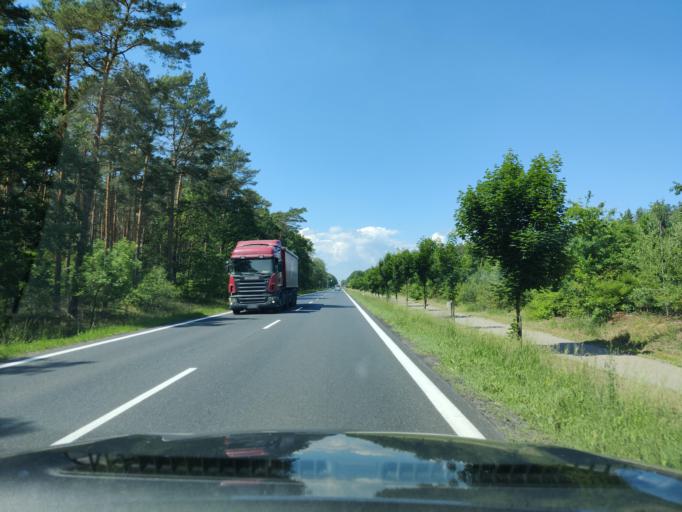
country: PL
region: Greater Poland Voivodeship
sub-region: Powiat wolsztynski
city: Wolsztyn
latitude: 52.1309
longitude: 16.1657
